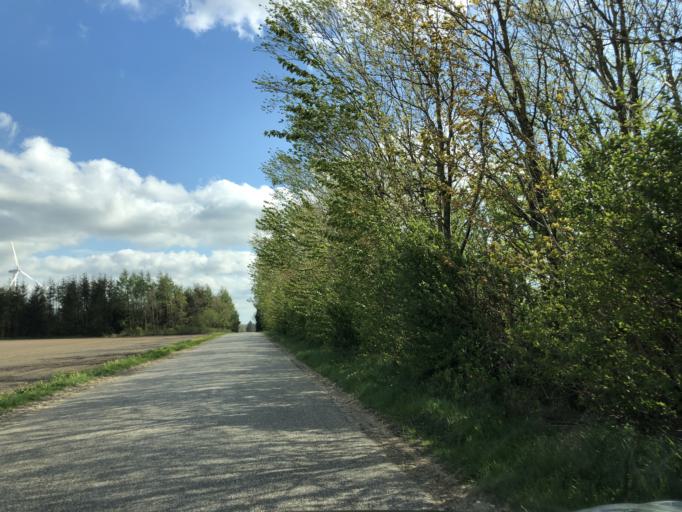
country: DK
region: Central Jutland
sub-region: Herning Kommune
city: Avlum
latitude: 56.2889
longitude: 8.6985
